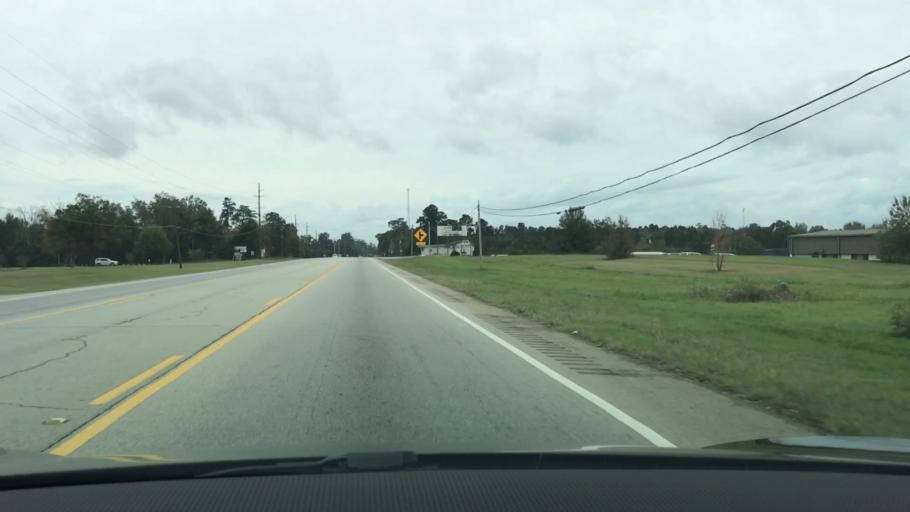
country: US
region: Georgia
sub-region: Jefferson County
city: Louisville
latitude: 33.0223
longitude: -82.4045
